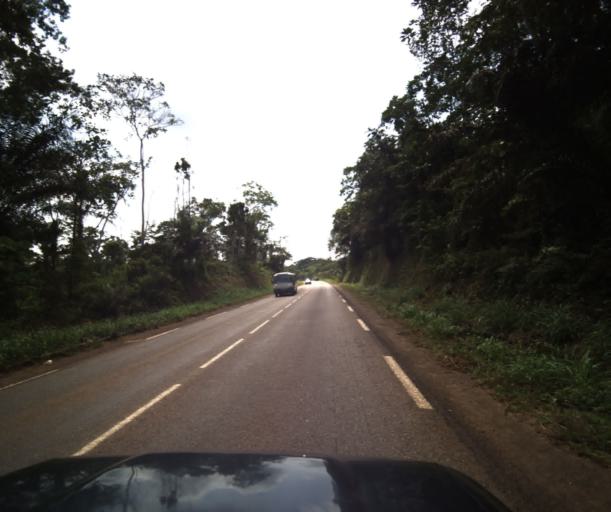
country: CM
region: Centre
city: Eseka
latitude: 3.8721
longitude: 10.6319
